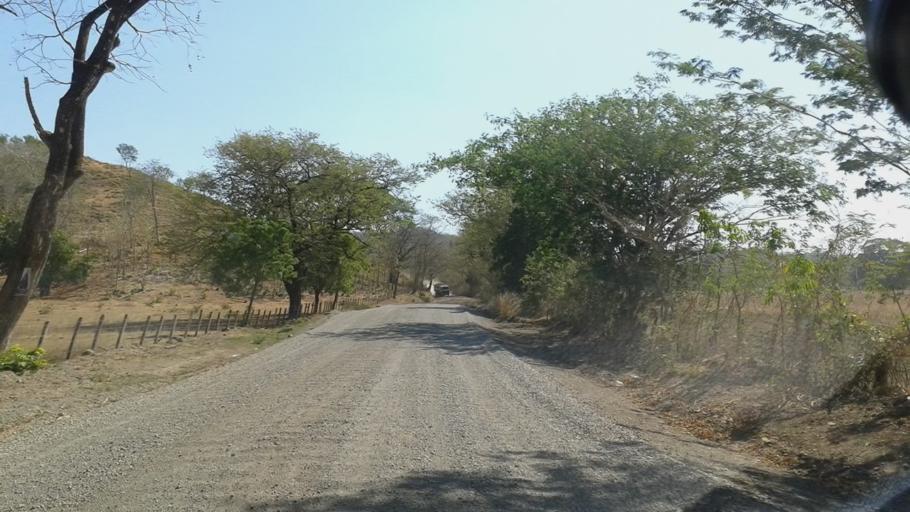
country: CR
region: Guanacaste
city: Santa Cruz
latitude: 10.1903
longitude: -85.7614
